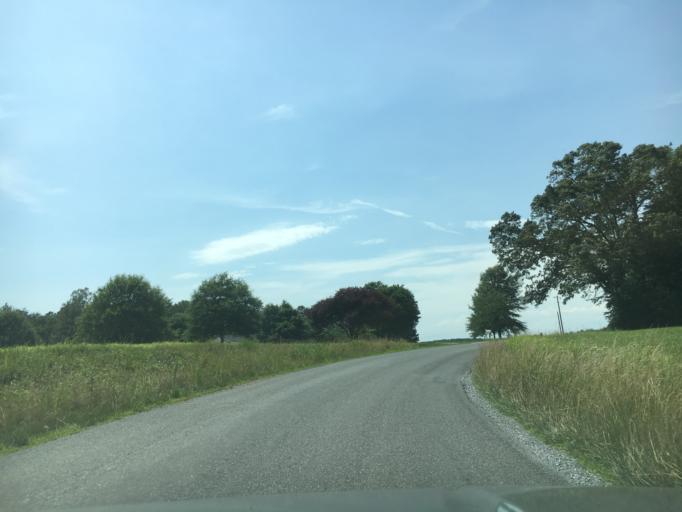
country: US
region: Virginia
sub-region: Pittsylvania County
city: Gretna
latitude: 36.9108
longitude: -79.4189
